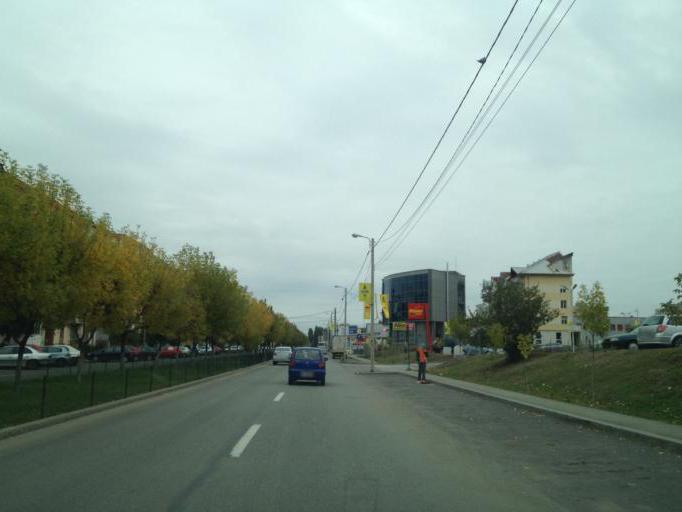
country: RO
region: Dolj
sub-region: Municipiul Craiova
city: Cernele
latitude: 44.3352
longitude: 23.7723
